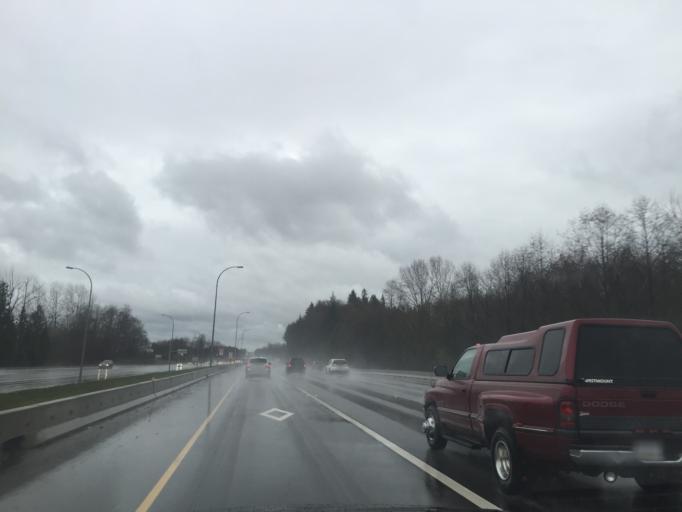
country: CA
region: British Columbia
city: Pitt Meadows
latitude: 49.1736
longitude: -122.7049
